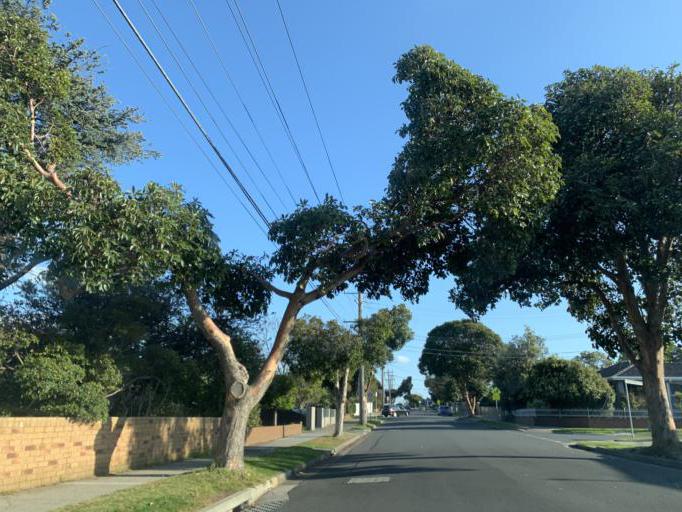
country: AU
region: Victoria
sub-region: Kingston
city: Mordialloc
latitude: -37.9856
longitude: 145.0894
